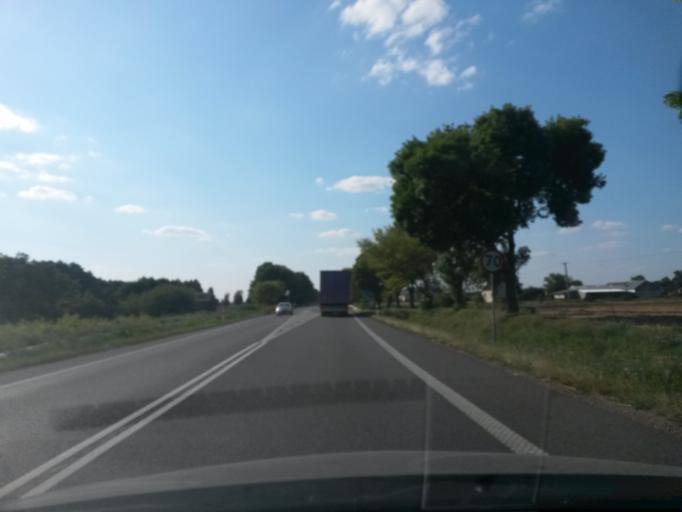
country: PL
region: Masovian Voivodeship
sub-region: Powiat sierpecki
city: Sierpc
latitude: 52.8431
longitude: 19.7212
